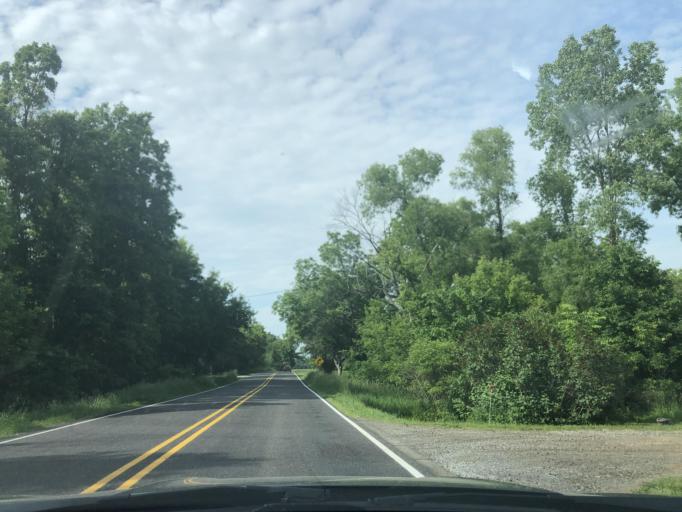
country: US
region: Michigan
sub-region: Clinton County
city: Bath
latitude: 42.8684
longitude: -84.4839
